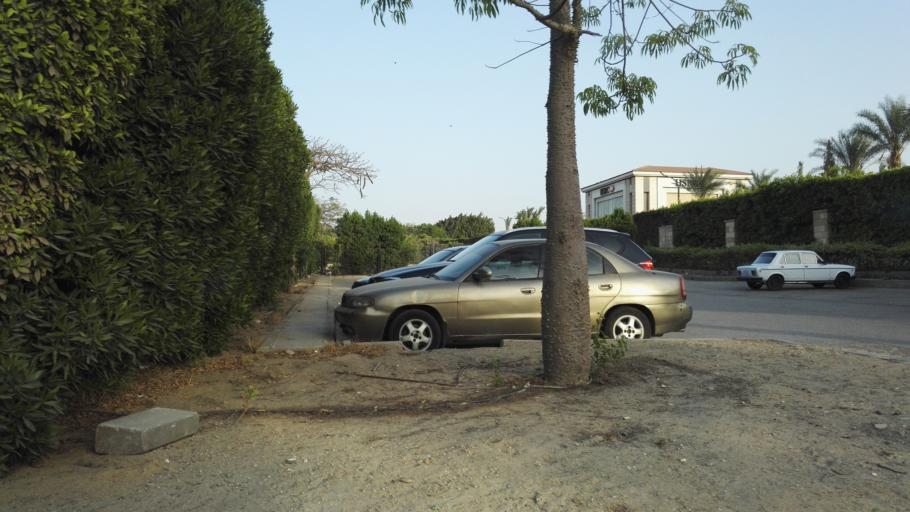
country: EG
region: Muhafazat al Qahirah
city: Cairo
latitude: 29.9969
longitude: 31.4082
